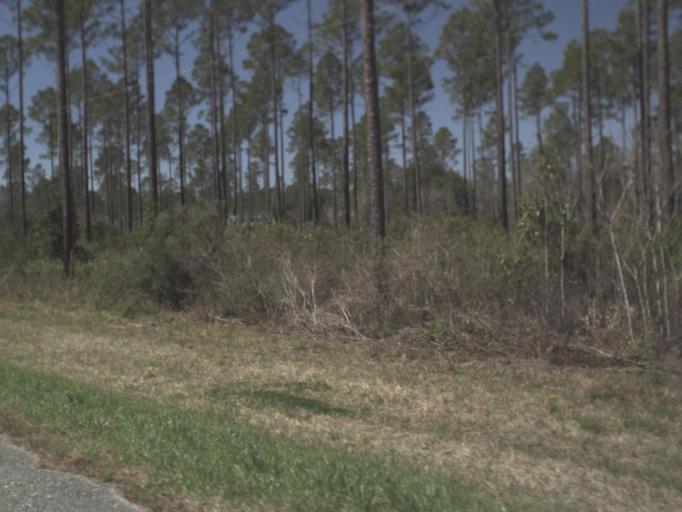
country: US
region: Florida
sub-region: Leon County
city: Woodville
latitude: 30.3270
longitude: -84.0296
